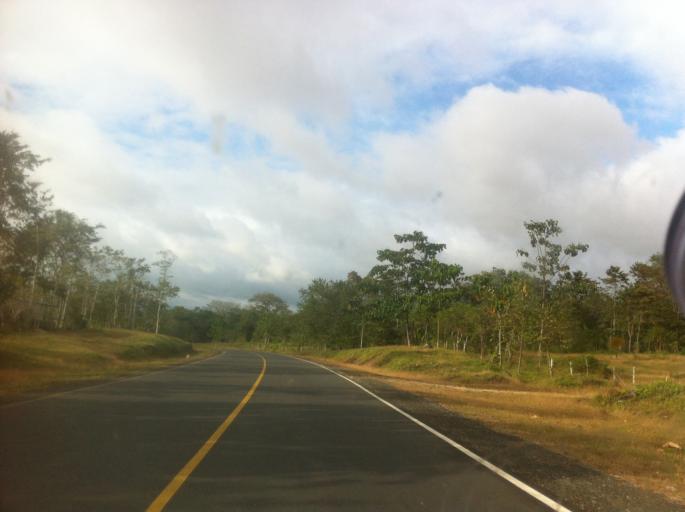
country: NI
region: Rio San Juan
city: San Carlos
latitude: 11.1989
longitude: -84.6807
